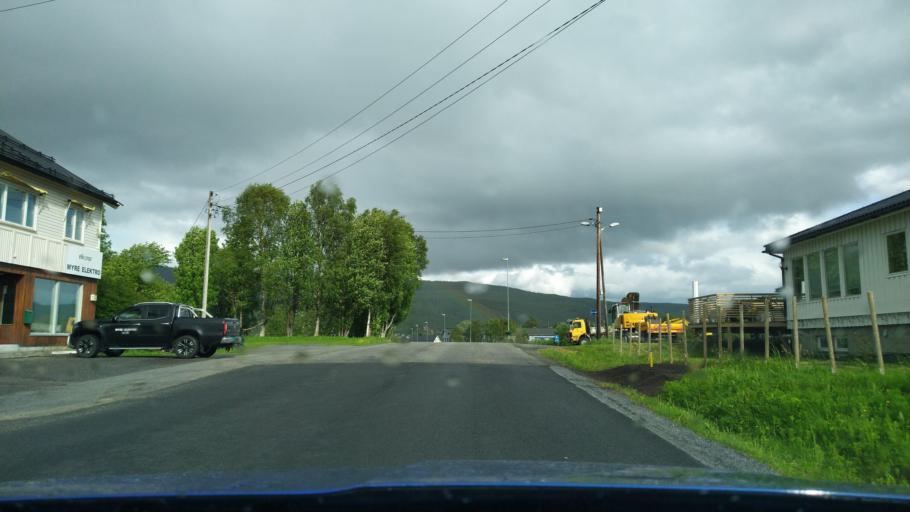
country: NO
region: Troms
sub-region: Sorreisa
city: Sorreisa
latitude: 69.1441
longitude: 18.1406
